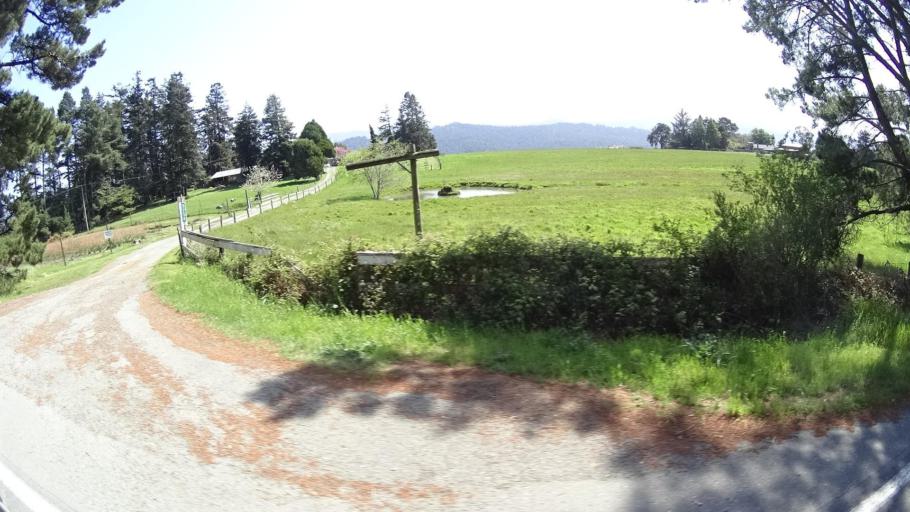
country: US
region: California
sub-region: Humboldt County
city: Hydesville
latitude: 40.5518
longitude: -124.1144
